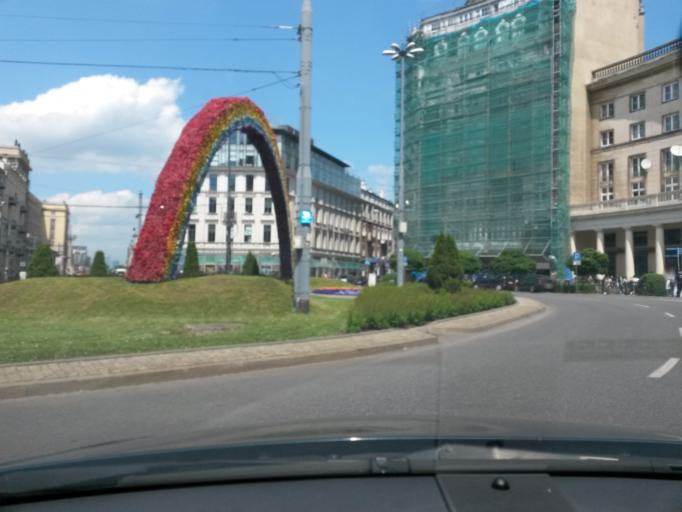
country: PL
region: Masovian Voivodeship
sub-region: Warszawa
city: Srodmiescie
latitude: 52.2196
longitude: 21.0182
